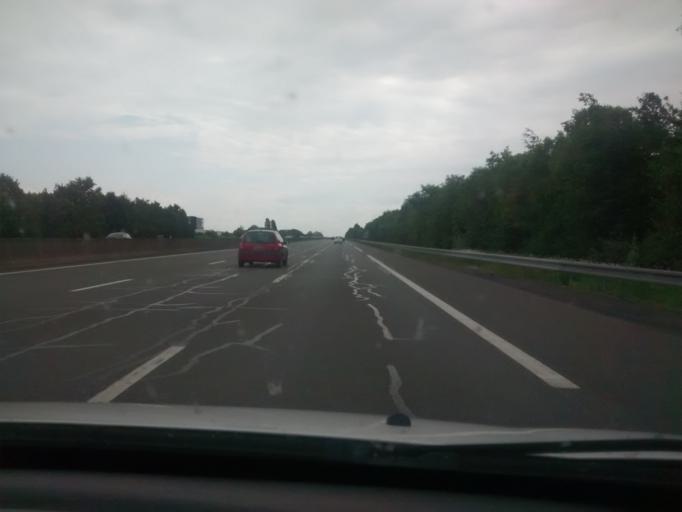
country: FR
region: Centre
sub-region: Departement d'Eure-et-Loir
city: Le Coudray
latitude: 48.4334
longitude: 1.5205
